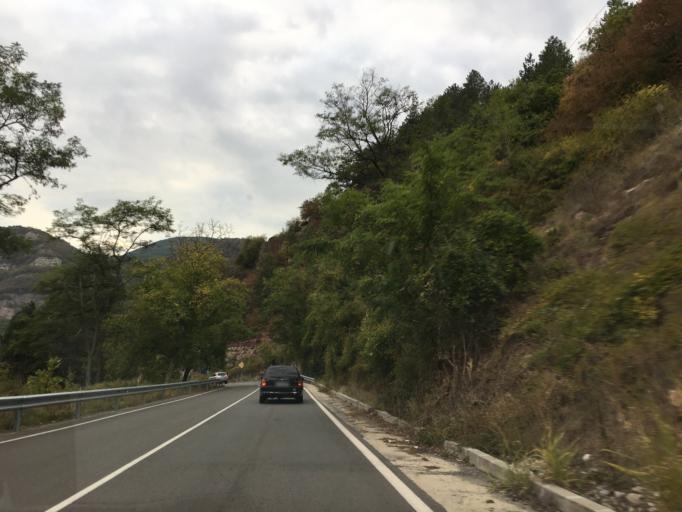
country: BG
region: Sofiya
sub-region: Obshtina Svoge
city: Bov
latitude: 43.0094
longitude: 23.3485
